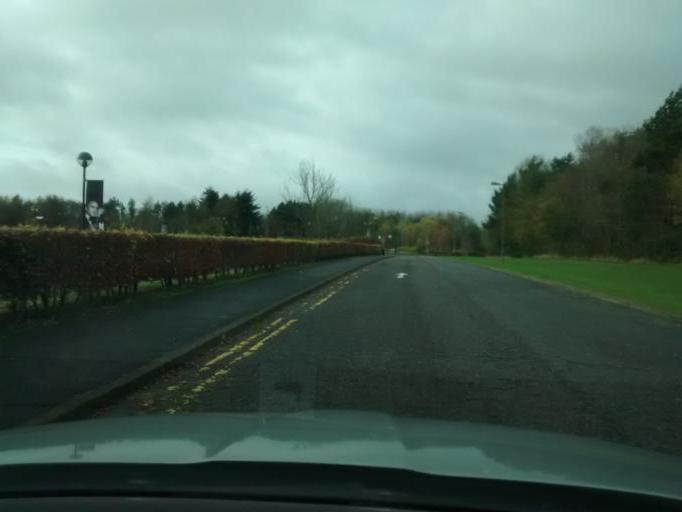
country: GB
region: Scotland
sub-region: West Lothian
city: West Calder
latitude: 55.8788
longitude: -3.5526
